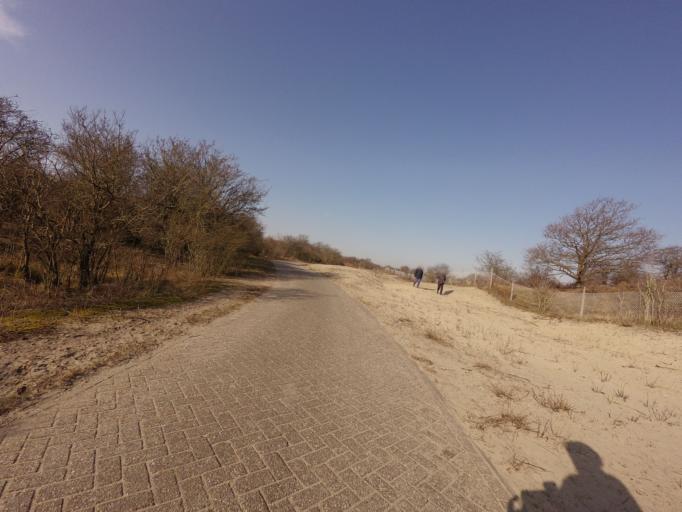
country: NL
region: North Holland
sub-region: Gemeente Zandvoort
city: Zandvoort
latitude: 52.3756
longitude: 4.5697
